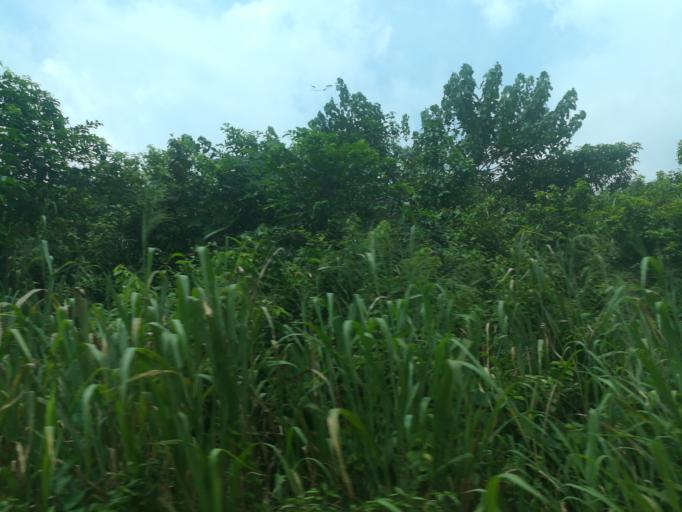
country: NG
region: Lagos
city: Ikorodu
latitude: 6.6729
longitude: 3.6585
